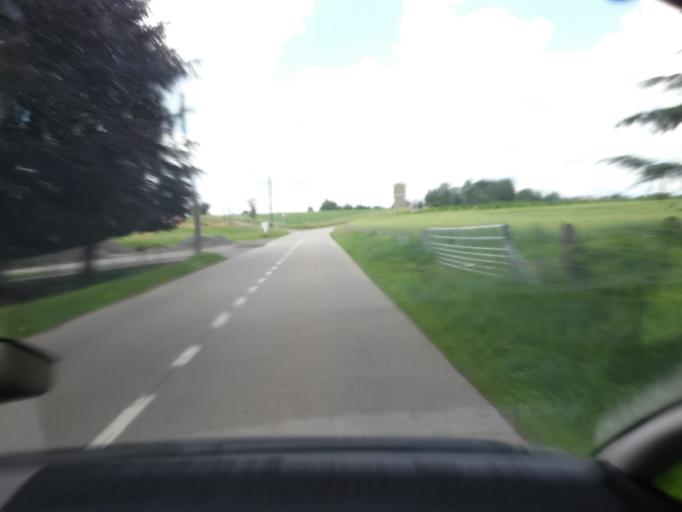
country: BE
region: Wallonia
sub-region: Province de Namur
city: Hamois
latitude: 50.2742
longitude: 5.1725
